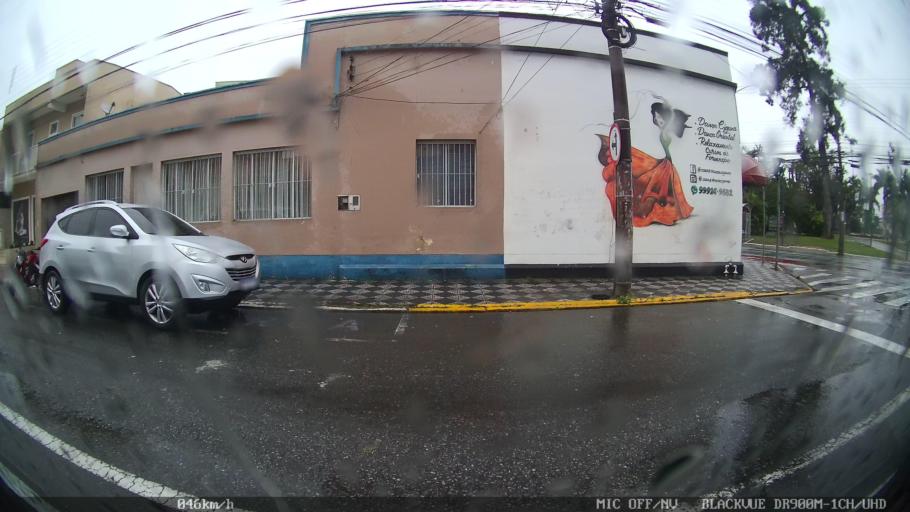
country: BR
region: Santa Catarina
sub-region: Itajai
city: Itajai
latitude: -26.9057
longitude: -48.6691
